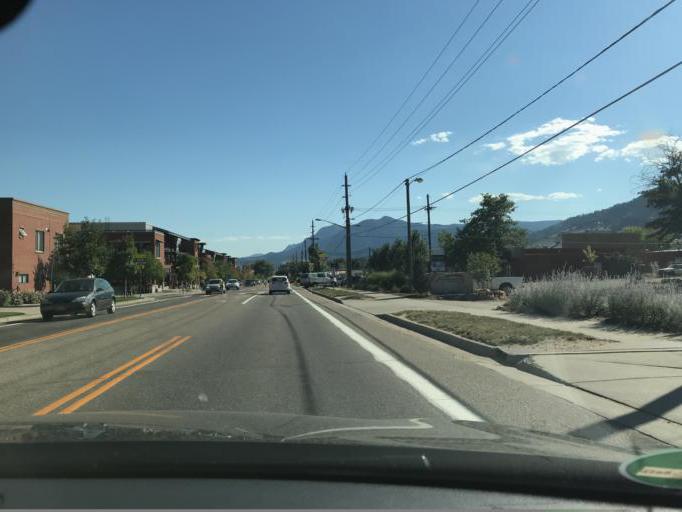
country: US
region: Colorado
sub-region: Boulder County
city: Boulder
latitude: 40.0589
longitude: -105.2822
